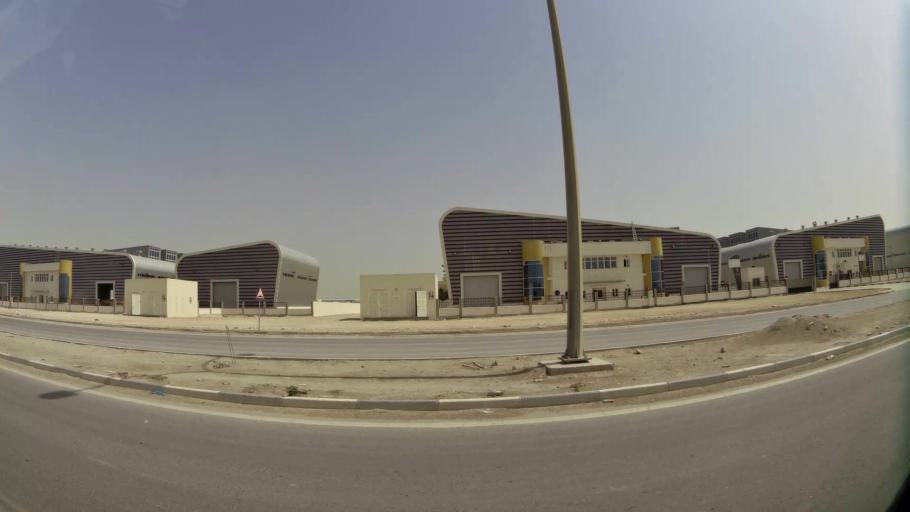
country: QA
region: Al Wakrah
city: Al Wukayr
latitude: 25.1653
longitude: 51.4207
